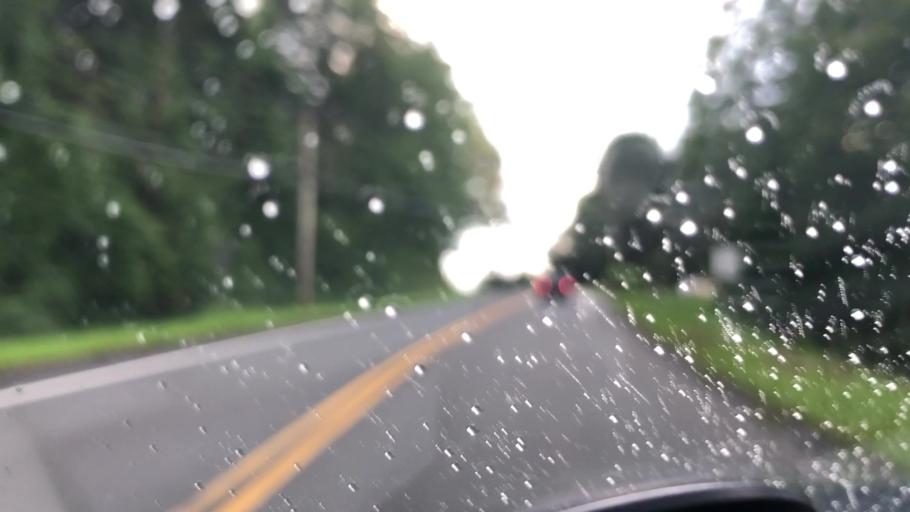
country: US
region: Massachusetts
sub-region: Hampshire County
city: Westhampton
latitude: 42.2873
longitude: -72.7585
